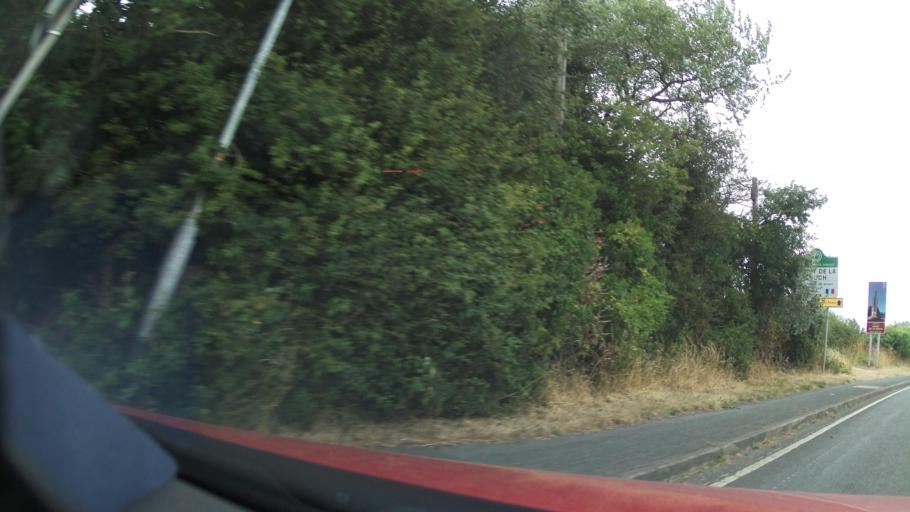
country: GB
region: England
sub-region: Leicestershire
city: Ashby de la Zouch
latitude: 52.7556
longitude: -1.4893
